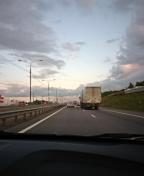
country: RU
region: Moskovskaya
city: Zhukovskiy
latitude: 55.5520
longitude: 38.0679
